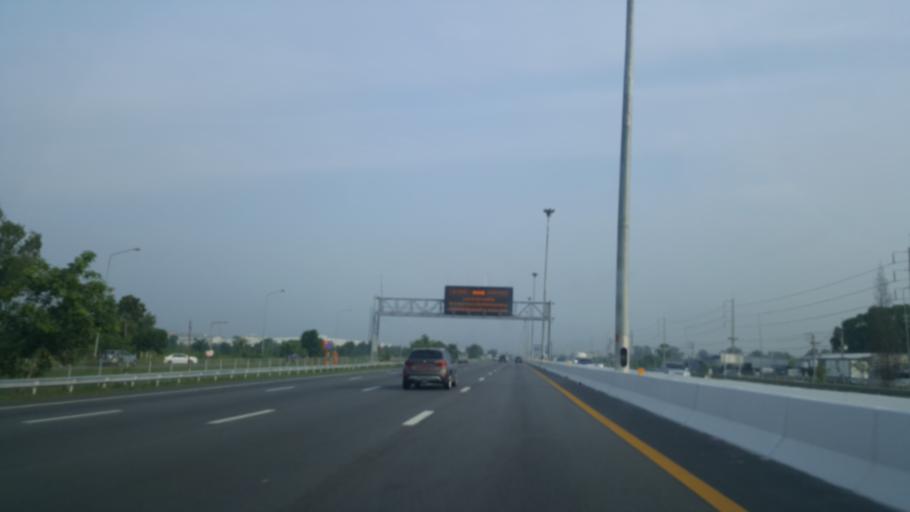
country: TH
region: Chon Buri
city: Phan Thong
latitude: 13.4189
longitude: 101.0469
